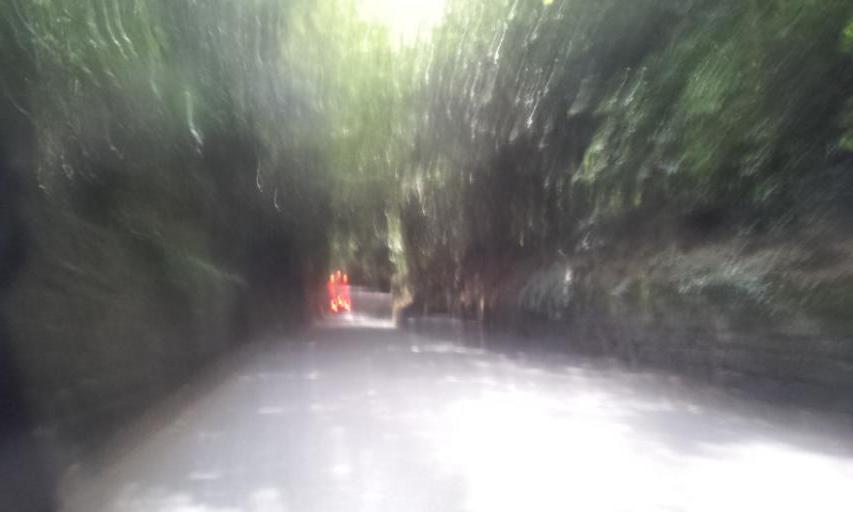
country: GB
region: England
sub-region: Kent
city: Pembury
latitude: 51.1382
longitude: 0.2926
